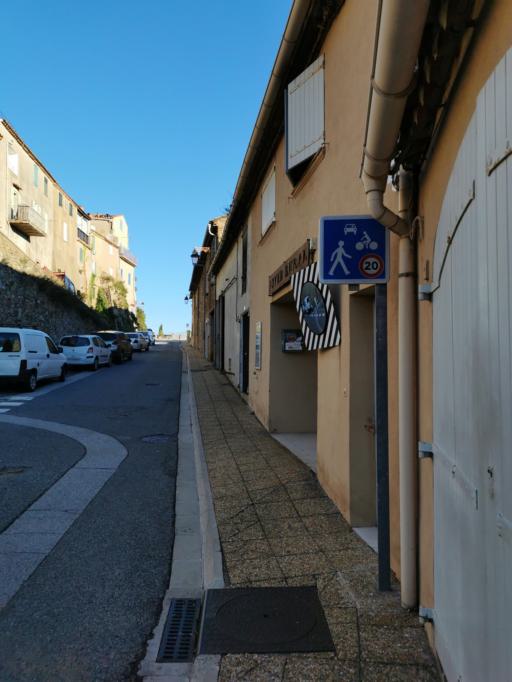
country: FR
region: Provence-Alpes-Cote d'Azur
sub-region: Departement du Var
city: Ramatuelle
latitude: 43.2146
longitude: 6.6135
